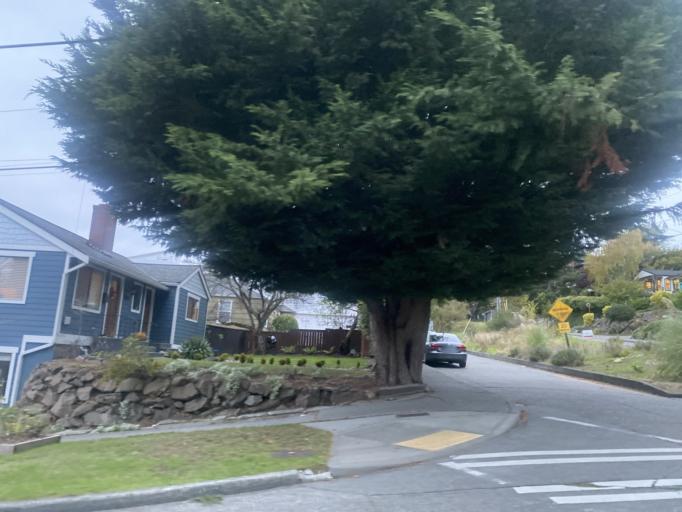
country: US
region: Washington
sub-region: King County
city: Seattle
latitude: 47.6468
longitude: -122.3958
